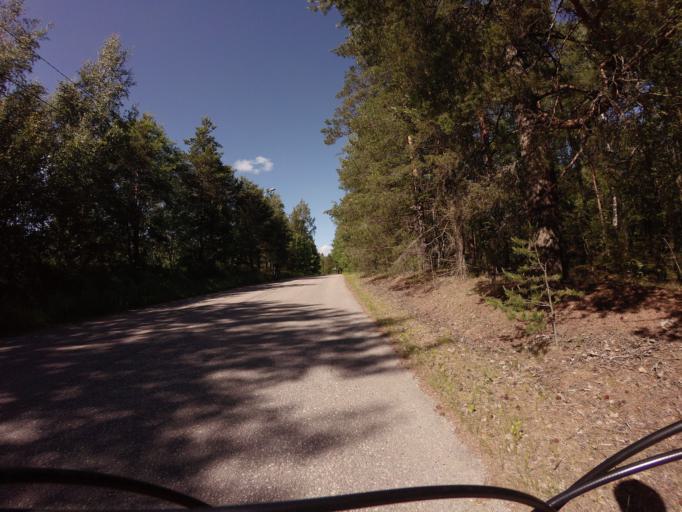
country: FI
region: Varsinais-Suomi
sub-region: Turku
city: Turku
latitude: 60.4944
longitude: 22.2794
